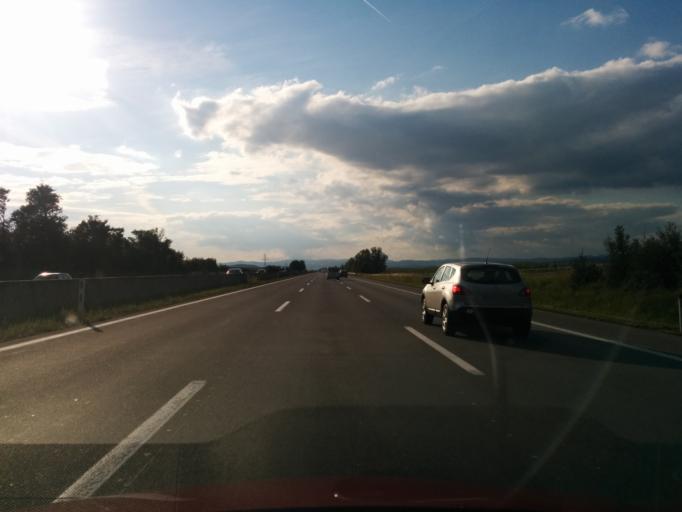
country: AT
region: Lower Austria
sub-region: Politischer Bezirk Sankt Polten
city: Haunoldstein
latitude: 48.1819
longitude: 15.4474
